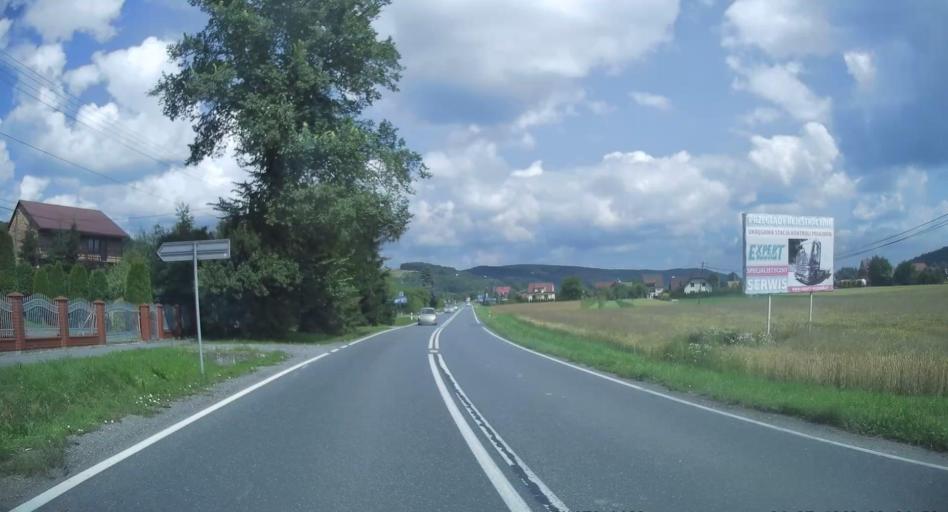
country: PL
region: Lesser Poland Voivodeship
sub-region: Powiat tarnowski
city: Zakliczyn
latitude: 49.8924
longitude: 20.8177
